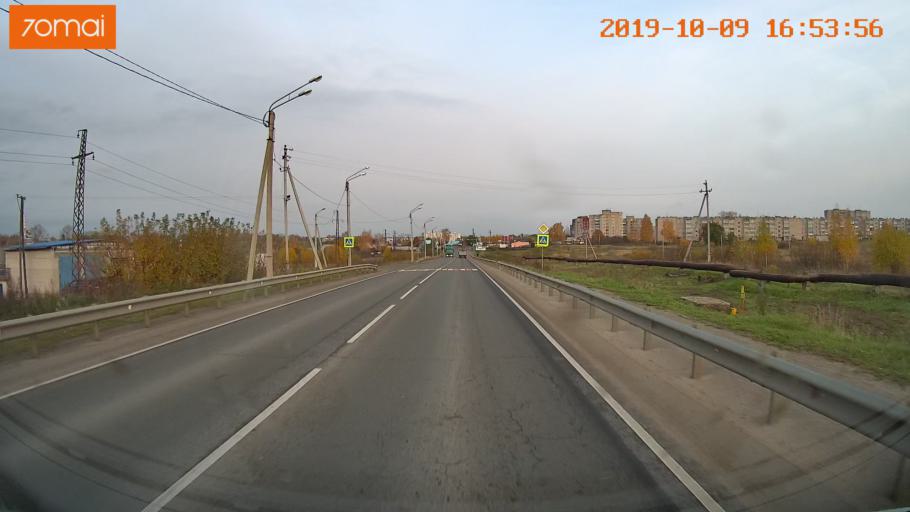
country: RU
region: Ivanovo
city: Privolzhsk
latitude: 57.3748
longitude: 41.2734
